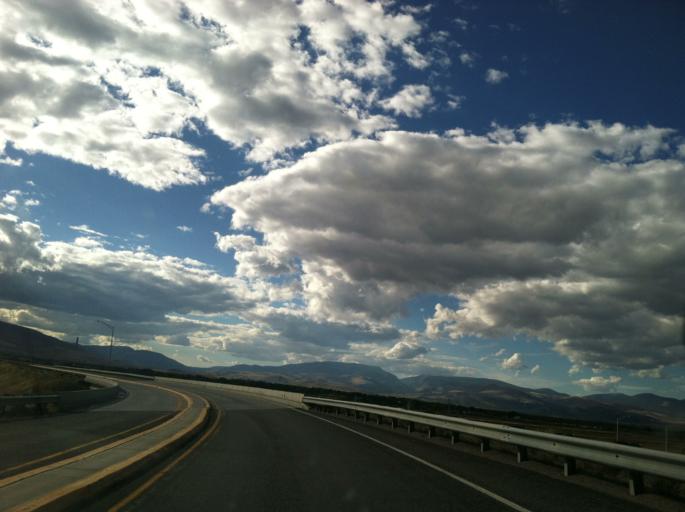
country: US
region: Montana
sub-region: Deer Lodge County
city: Warm Springs
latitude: 46.0922
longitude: -112.7903
